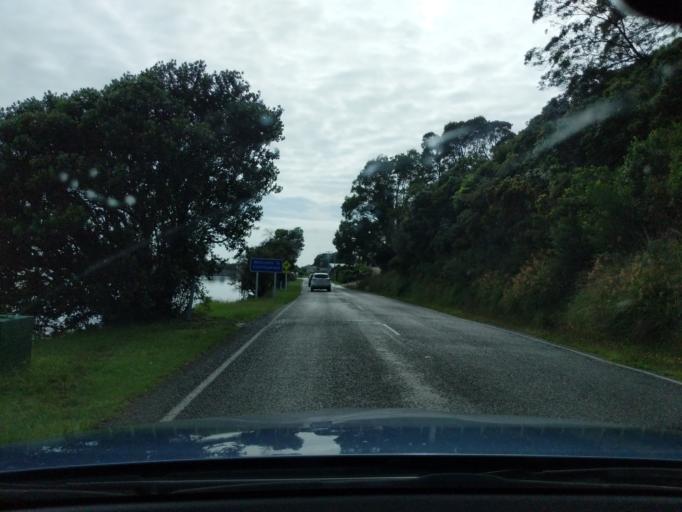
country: NZ
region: Tasman
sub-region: Tasman District
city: Takaka
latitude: -40.6799
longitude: 172.6776
